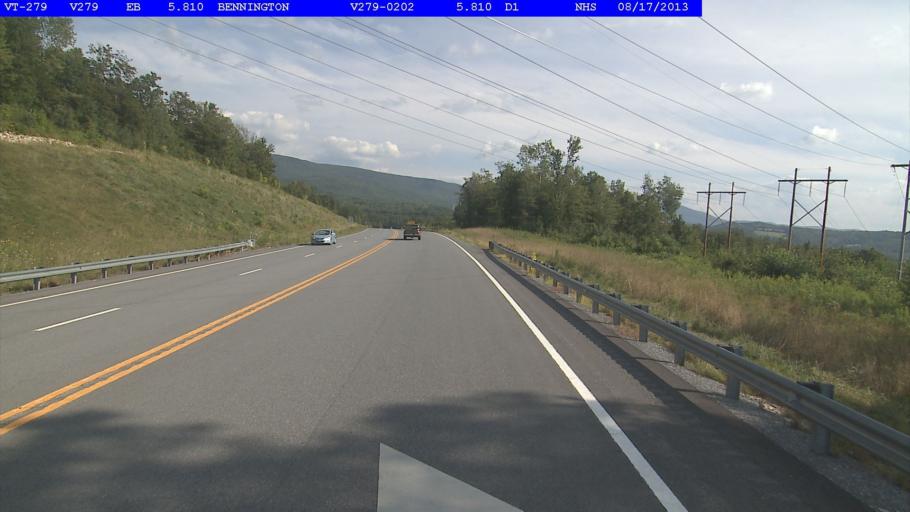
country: US
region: Vermont
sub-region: Bennington County
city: Bennington
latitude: 42.8900
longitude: -73.1758
